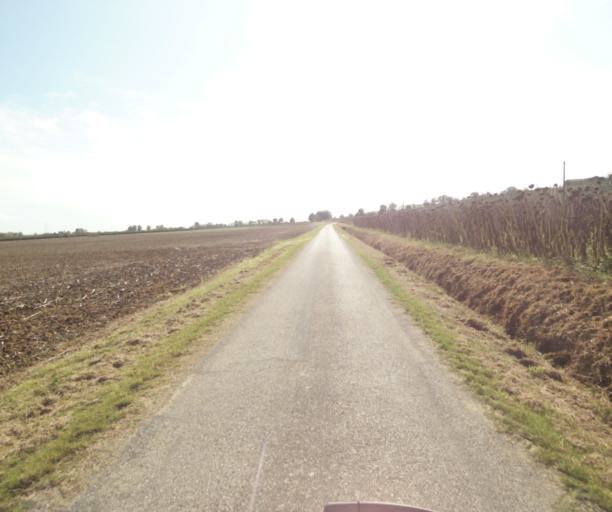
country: FR
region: Midi-Pyrenees
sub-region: Departement du Tarn-et-Garonne
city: Verdun-sur-Garonne
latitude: 43.8526
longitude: 1.1944
